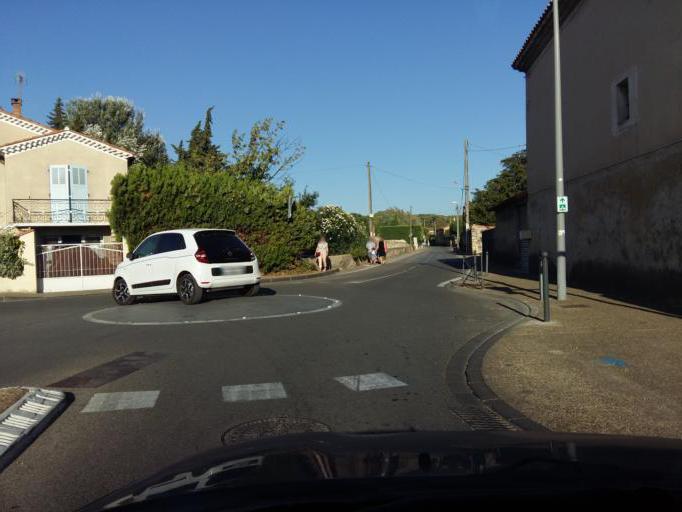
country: FR
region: Provence-Alpes-Cote d'Azur
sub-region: Departement du Vaucluse
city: Carpentras
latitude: 44.0513
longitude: 5.0563
